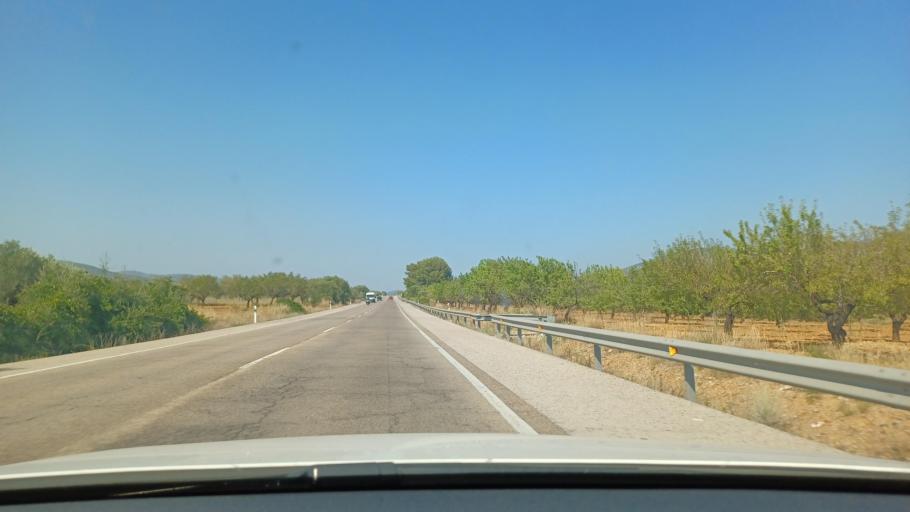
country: ES
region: Valencia
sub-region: Provincia de Castello
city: Alcala de Xivert
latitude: 40.3247
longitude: 0.2437
